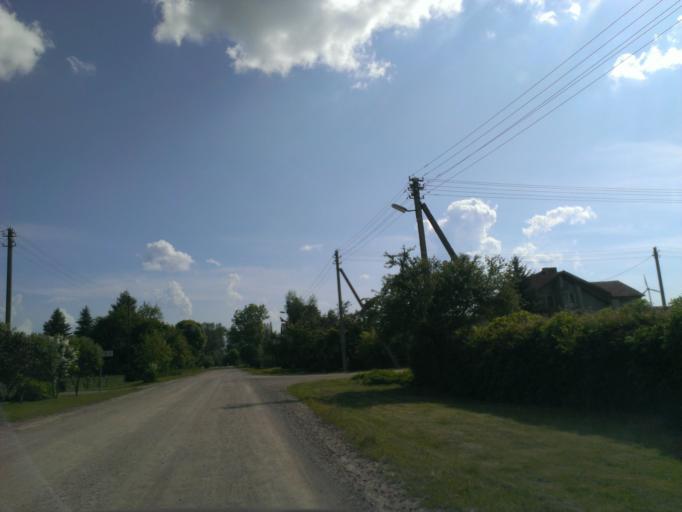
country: LT
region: Klaipedos apskritis
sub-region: Klaipeda
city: Palanga
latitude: 55.9042
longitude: 21.1334
